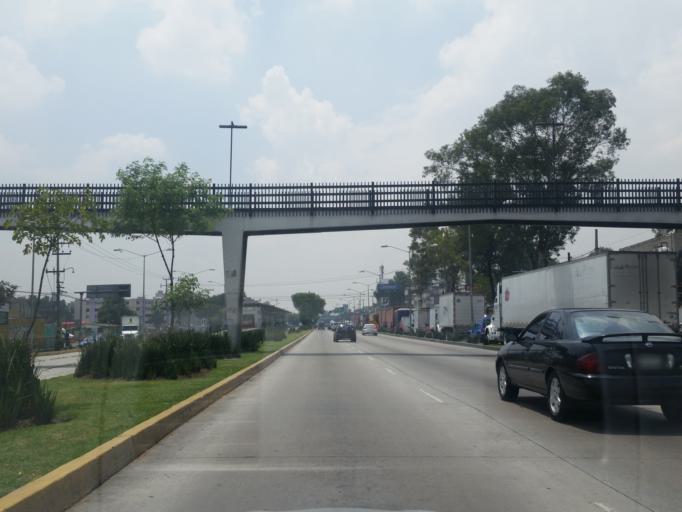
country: MX
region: Mexico City
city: Azcapotzalco
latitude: 19.5101
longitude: -99.1600
